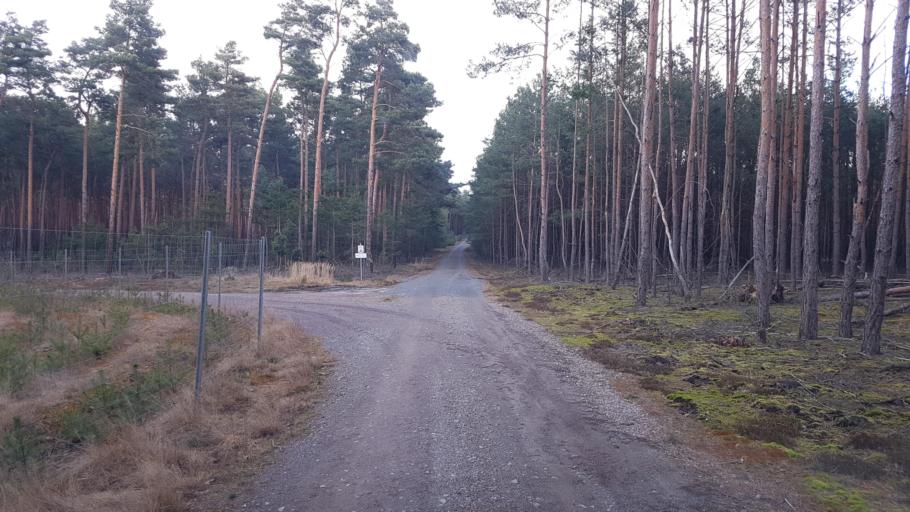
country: DE
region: Brandenburg
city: Schlieben
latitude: 51.6723
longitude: 13.3974
